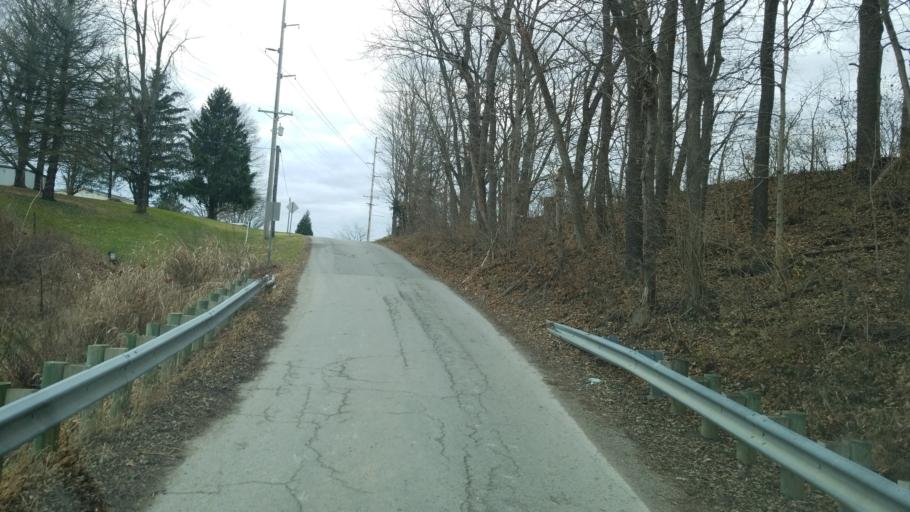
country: US
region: Ohio
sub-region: Highland County
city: Greenfield
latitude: 39.3341
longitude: -83.3147
